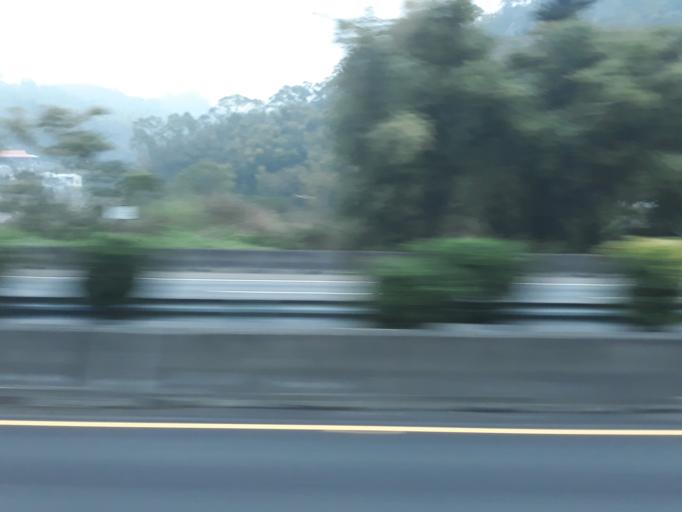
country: TW
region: Taiwan
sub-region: Miaoli
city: Miaoli
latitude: 24.5943
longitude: 120.8604
